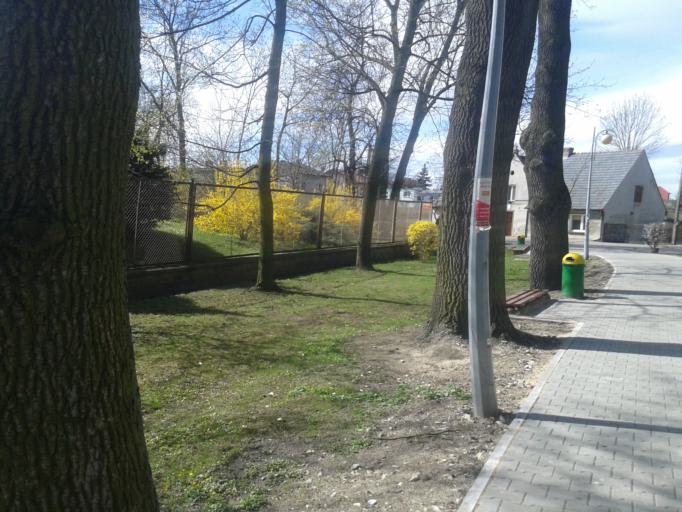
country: PL
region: Lower Silesian Voivodeship
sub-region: Powiat olesnicki
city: Miedzyborz
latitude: 51.3966
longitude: 17.6646
